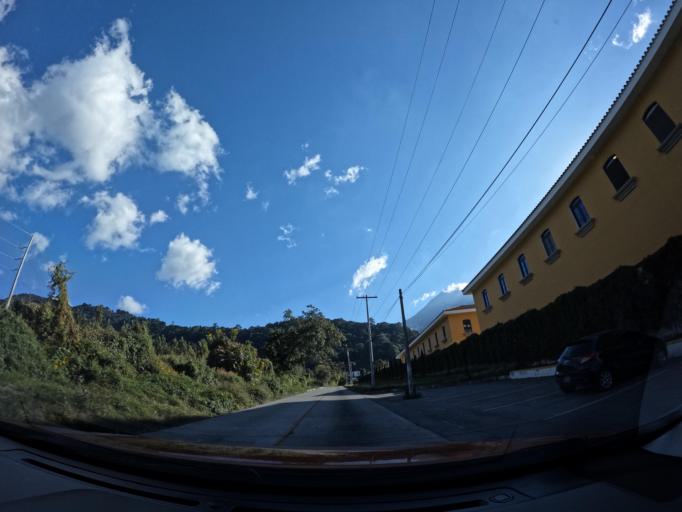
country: GT
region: Sacatepequez
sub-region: Municipio de Santa Maria de Jesus
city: Santa Maria de Jesus
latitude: 14.5164
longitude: -90.7223
